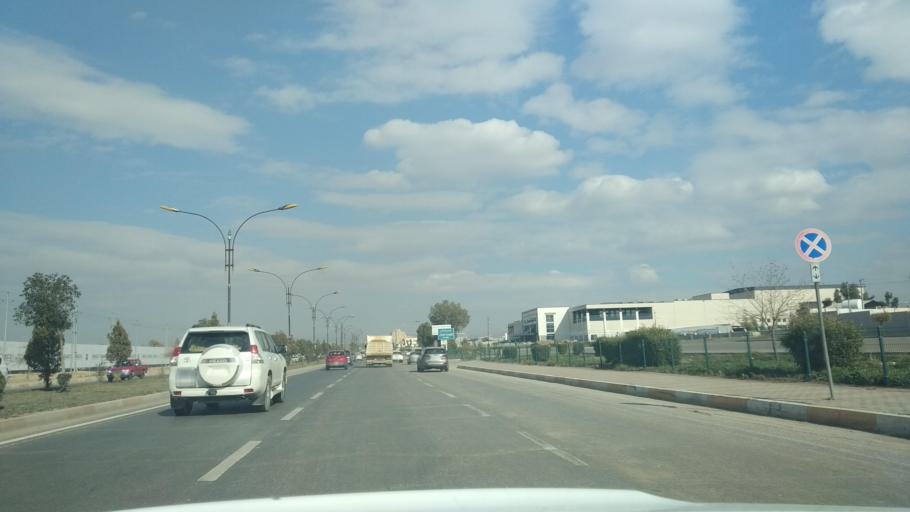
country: IQ
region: Arbil
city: Erbil
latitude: 36.2516
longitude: 44.0774
